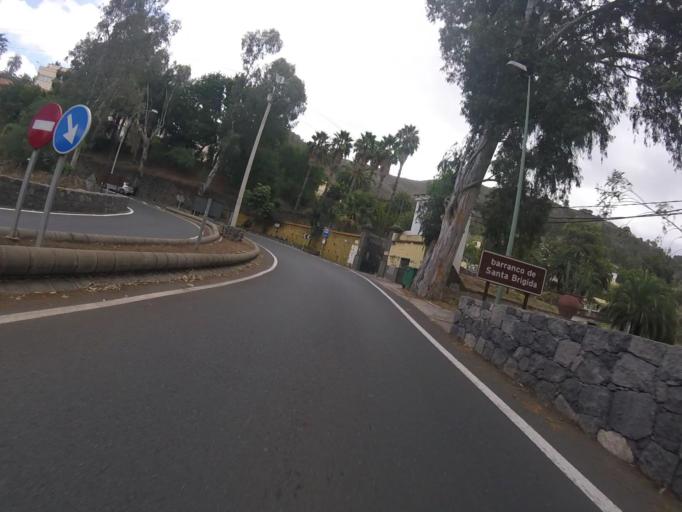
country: ES
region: Canary Islands
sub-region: Provincia de Las Palmas
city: Santa Brigida
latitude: 28.0270
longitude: -15.5008
